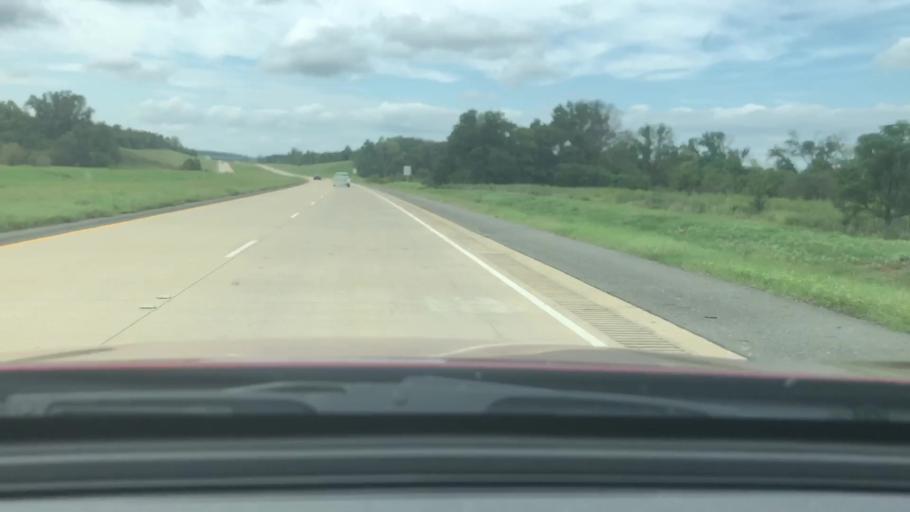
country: US
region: Louisiana
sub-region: Caddo Parish
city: Vivian
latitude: 32.9085
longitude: -93.8683
